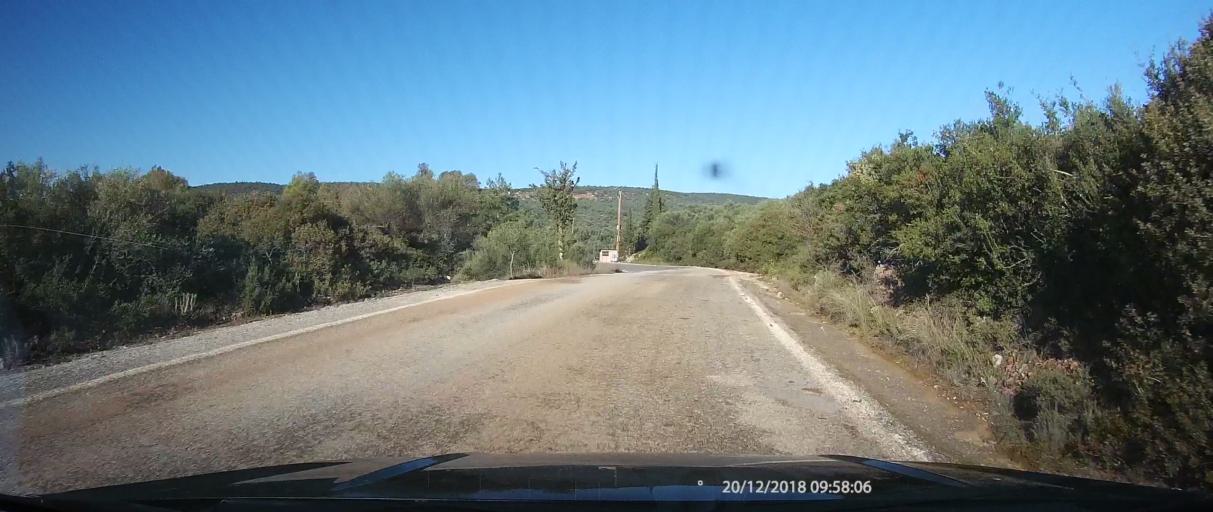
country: GR
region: Peloponnese
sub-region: Nomos Lakonias
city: Yerakion
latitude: 37.0220
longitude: 22.5892
